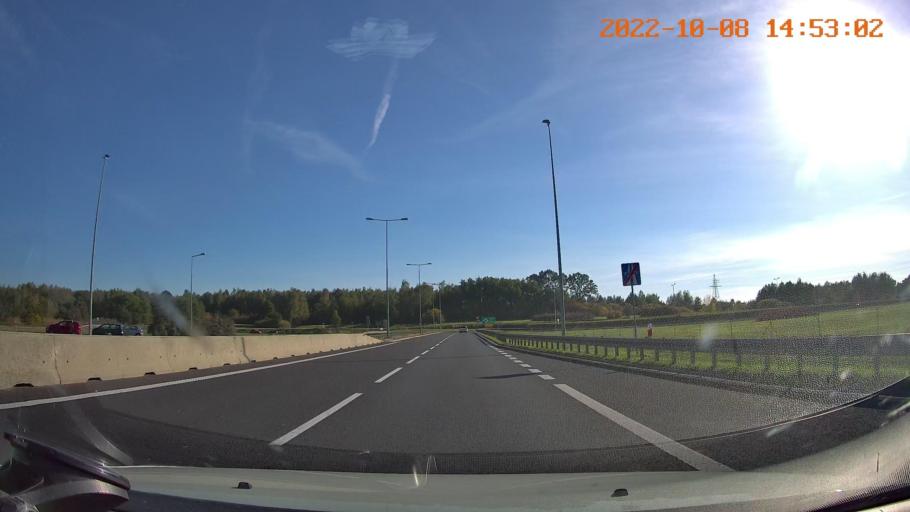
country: PL
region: Lesser Poland Voivodeship
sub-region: Powiat tarnowski
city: Lisia Gora
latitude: 50.0530
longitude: 21.0221
